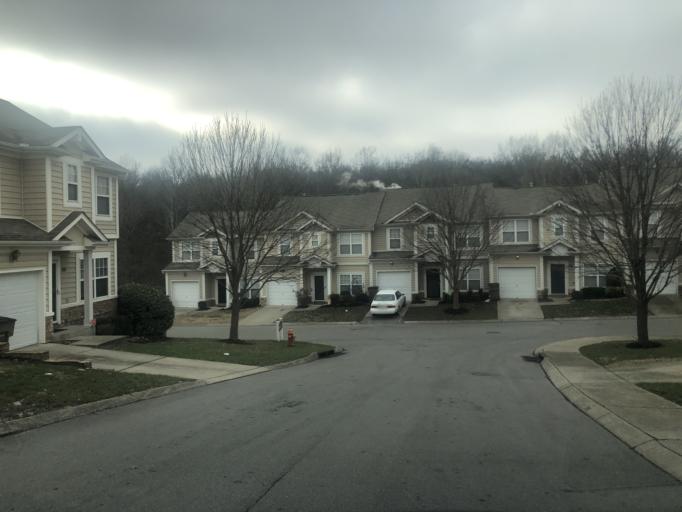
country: US
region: Tennessee
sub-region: Rutherford County
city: La Vergne
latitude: 36.0644
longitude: -86.6464
